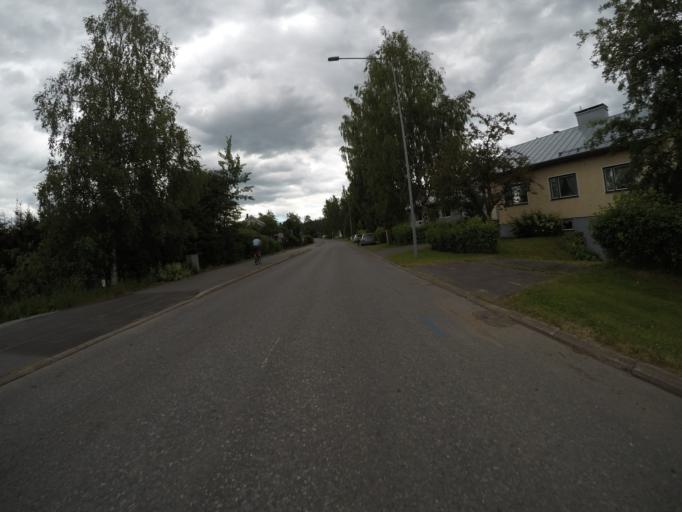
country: FI
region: Haeme
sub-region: Haemeenlinna
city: Haemeenlinna
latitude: 60.9830
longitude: 24.4392
